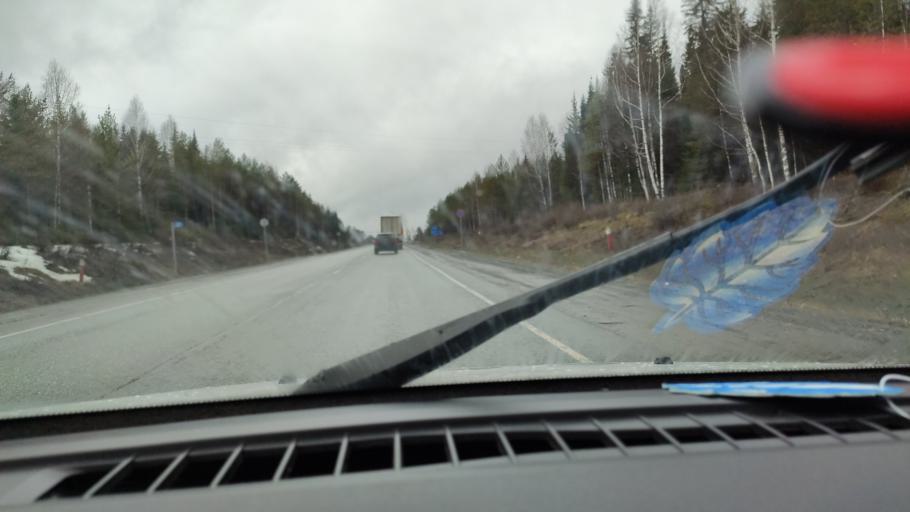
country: RU
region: Sverdlovsk
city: Druzhinino
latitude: 56.7963
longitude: 59.4220
